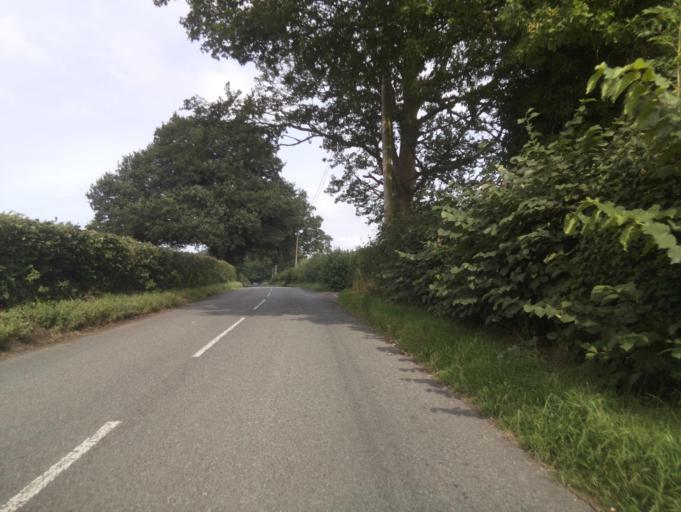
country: GB
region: England
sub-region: Bath and North East Somerset
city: East Harptree
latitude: 51.3009
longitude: -2.6093
